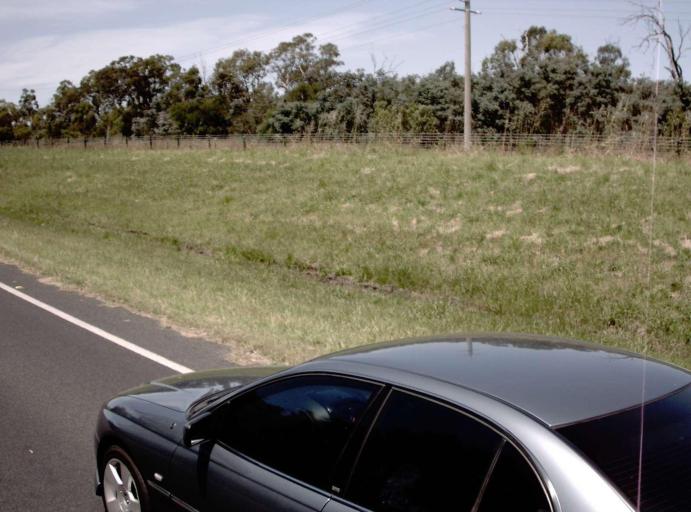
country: AU
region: Victoria
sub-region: Latrobe
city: Traralgon
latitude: -38.2104
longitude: 146.4887
